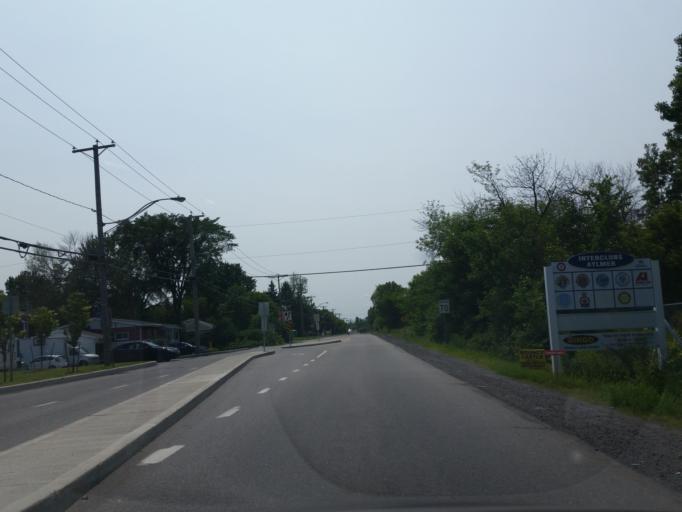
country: CA
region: Ontario
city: Bells Corners
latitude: 45.3866
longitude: -75.8055
